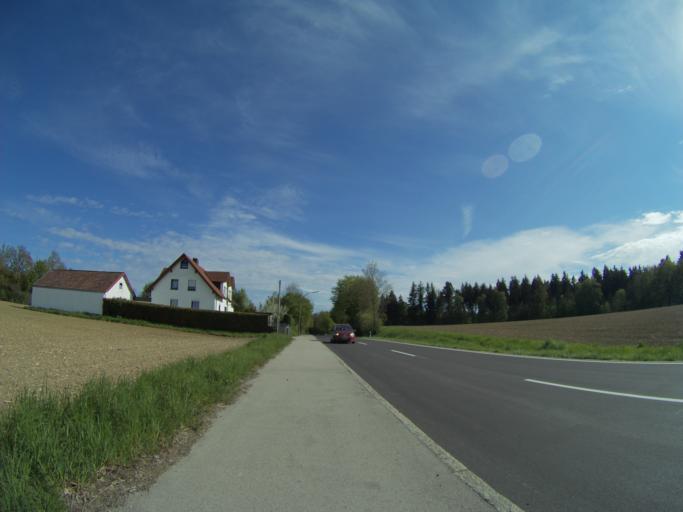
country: DE
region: Bavaria
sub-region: Upper Bavaria
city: Freising
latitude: 48.4227
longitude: 11.7336
